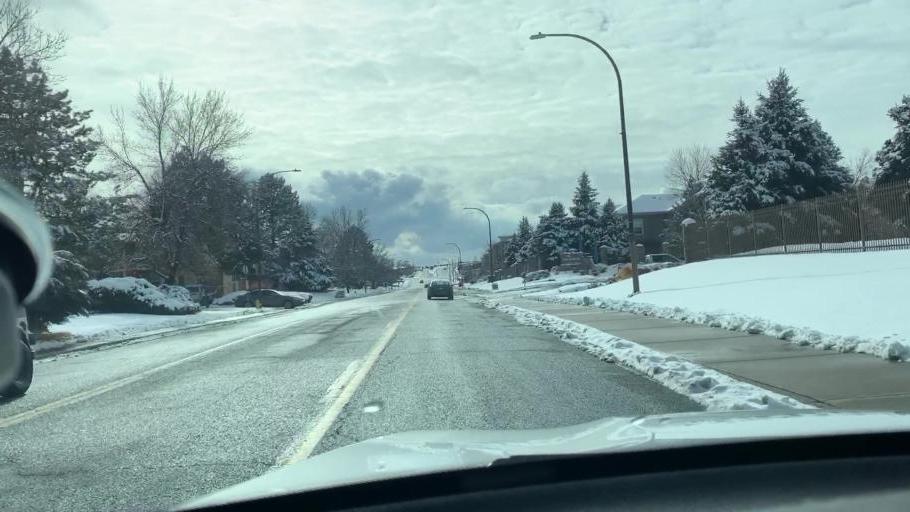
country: US
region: Colorado
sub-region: Adams County
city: Northglenn
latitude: 39.9078
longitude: -104.9874
